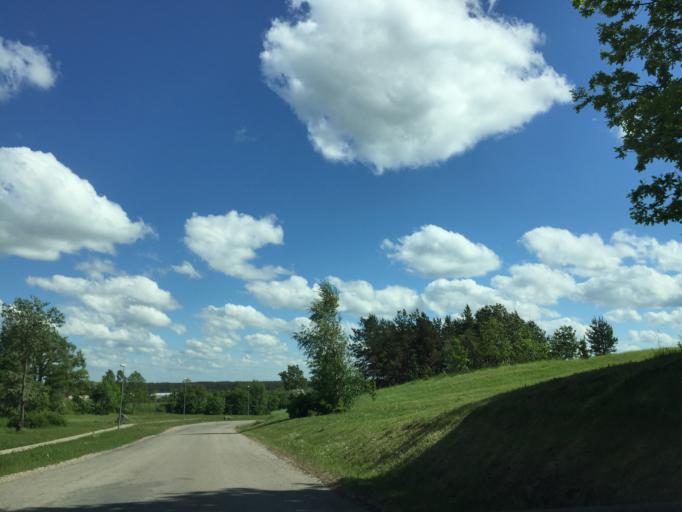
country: LV
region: Kandava
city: Kandava
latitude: 57.0432
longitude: 22.7805
